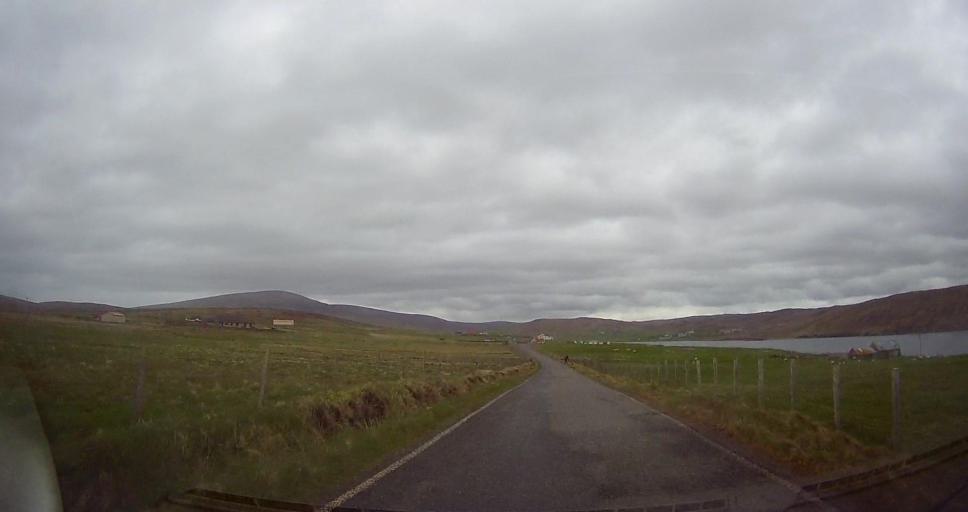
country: GB
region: Scotland
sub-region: Shetland Islands
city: Lerwick
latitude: 60.4791
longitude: -1.4805
